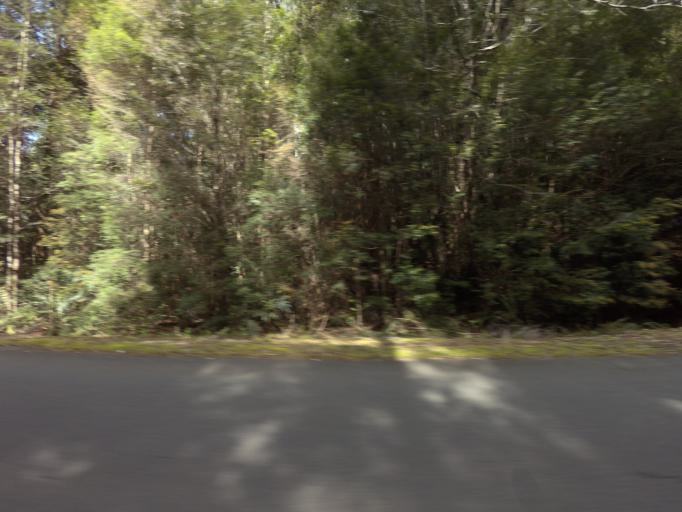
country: AU
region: Tasmania
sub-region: Huon Valley
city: Geeveston
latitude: -42.8220
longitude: 146.3118
